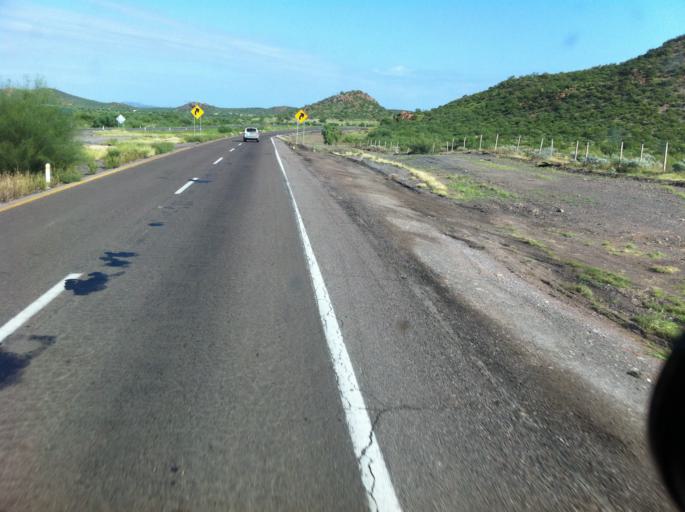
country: MX
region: Sonora
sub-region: Empalme
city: La Palma
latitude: 28.4522
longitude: -111.0464
